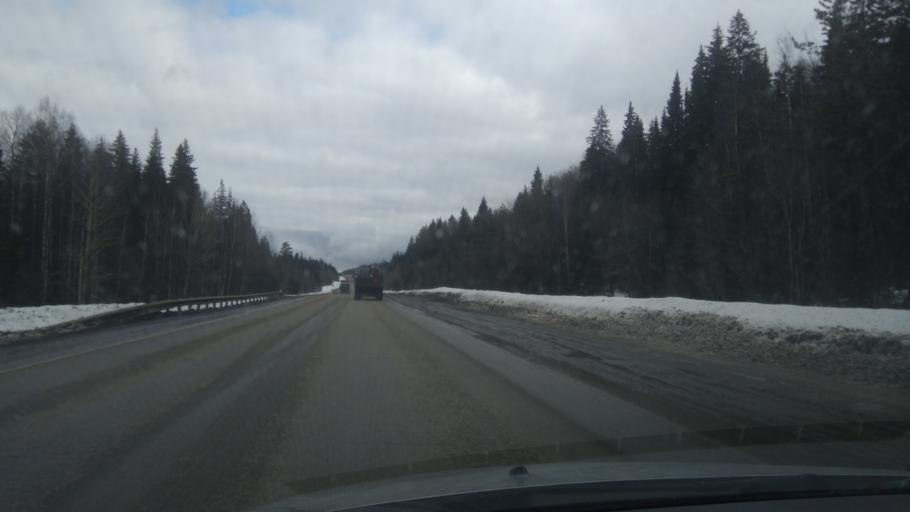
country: RU
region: Sverdlovsk
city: Bisert'
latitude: 56.8267
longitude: 59.2170
